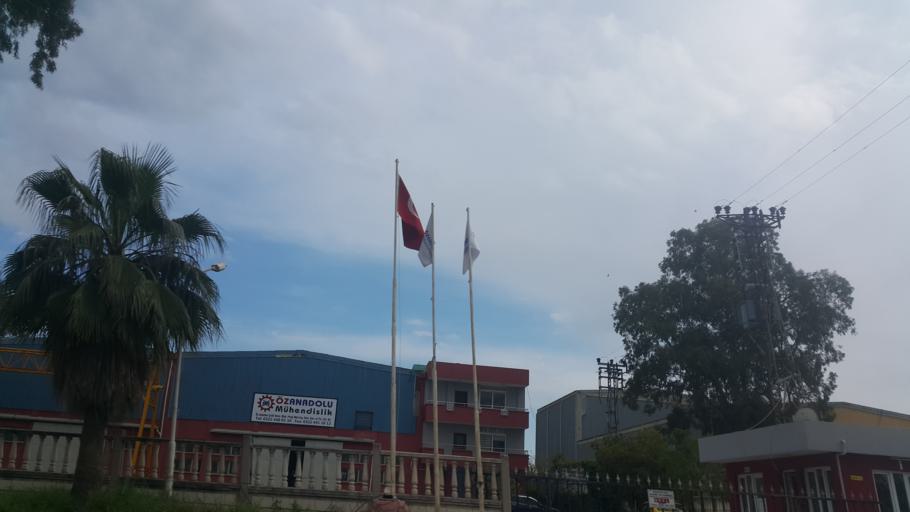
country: TR
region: Mersin
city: Yenice
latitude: 36.9918
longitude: 35.1776
